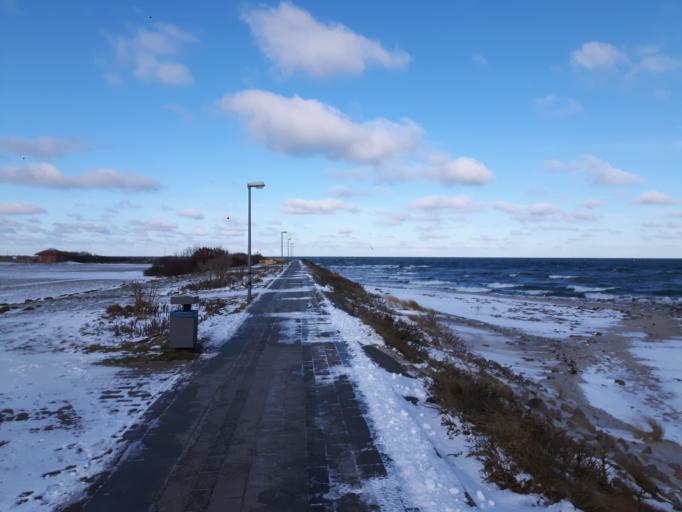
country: DE
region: Schleswig-Holstein
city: Heiligenhafen
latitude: 54.3830
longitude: 10.9535
